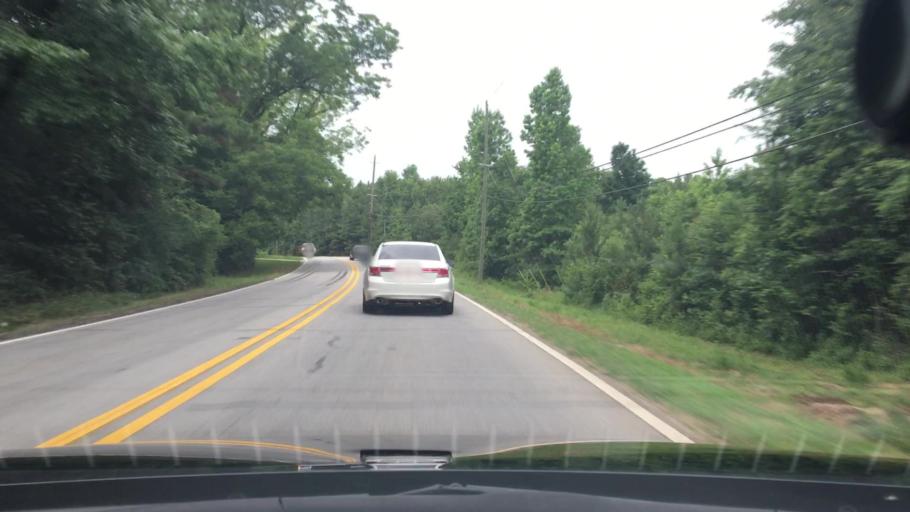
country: US
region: Georgia
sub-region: Coweta County
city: East Newnan
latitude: 33.3545
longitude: -84.7042
